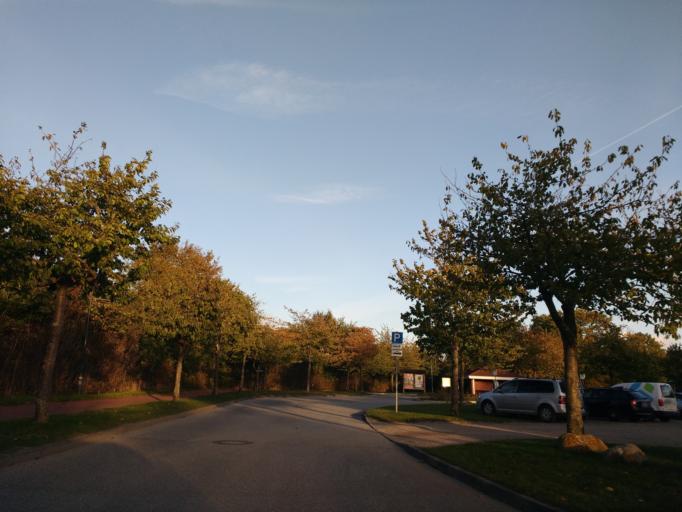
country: DE
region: Schleswig-Holstein
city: Kellenhusen
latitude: 54.1902
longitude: 11.0549
